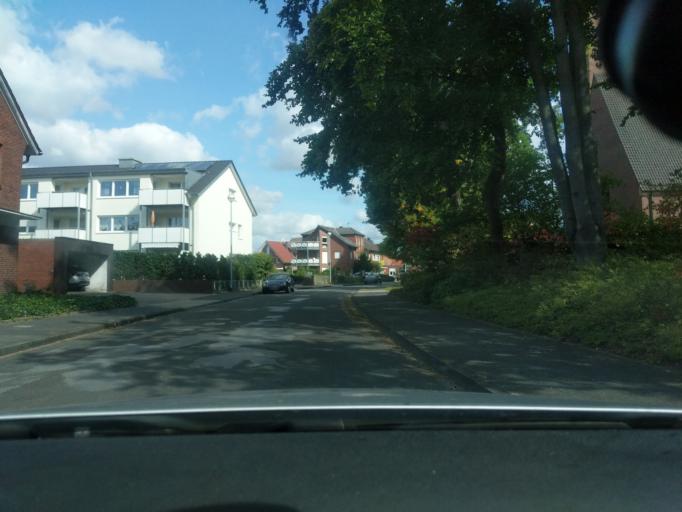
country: DE
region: North Rhine-Westphalia
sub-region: Regierungsbezirk Munster
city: Greven
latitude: 52.0879
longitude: 7.6178
